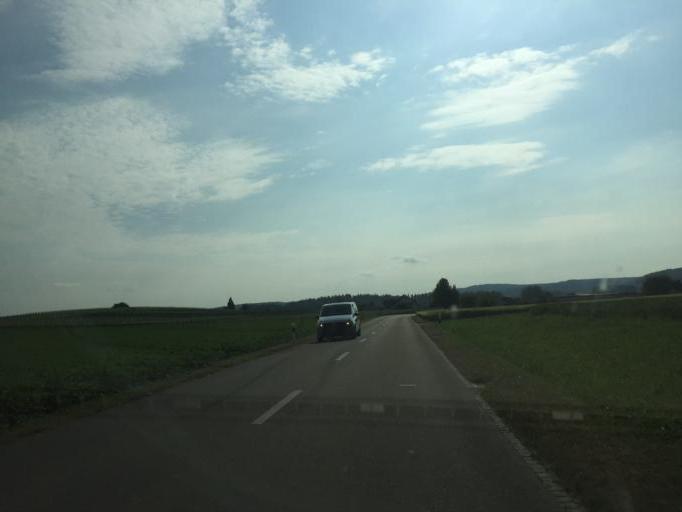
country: CH
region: Zurich
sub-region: Bezirk Buelach
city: Freienstein
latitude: 47.5690
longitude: 8.5885
